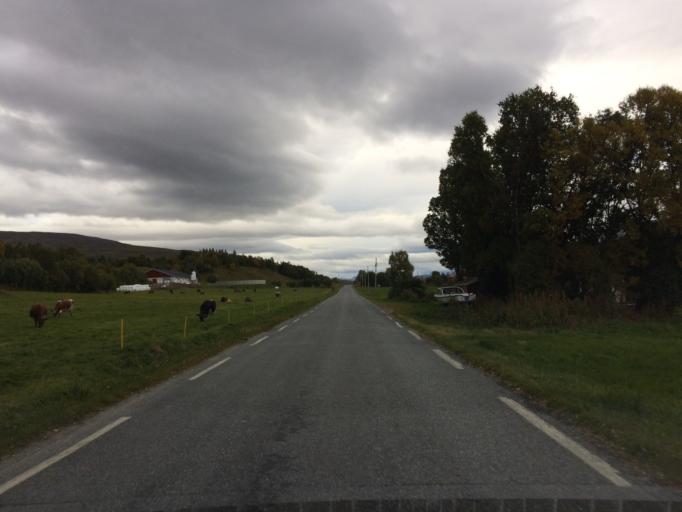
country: NO
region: Troms
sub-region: Sorreisa
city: Sorreisa
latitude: 69.5250
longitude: 18.2535
